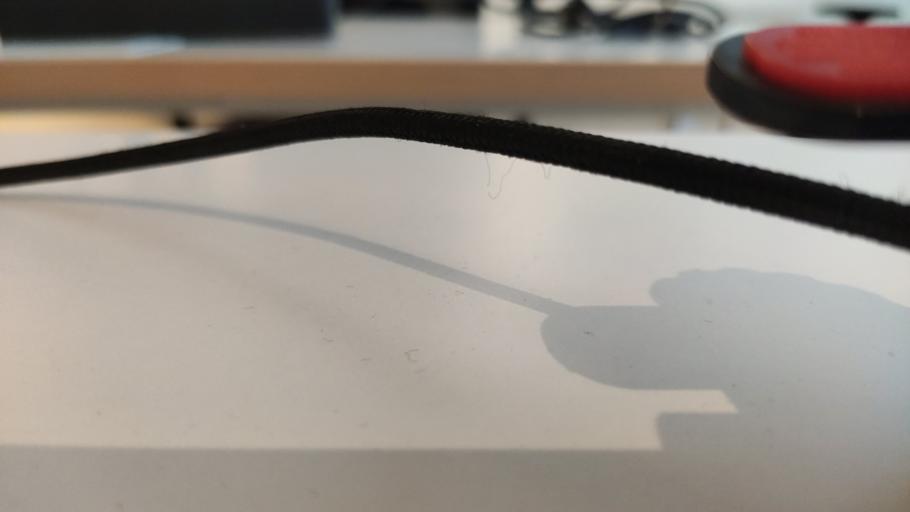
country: RU
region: Moskovskaya
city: Novopetrovskoye
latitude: 55.9397
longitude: 36.4355
